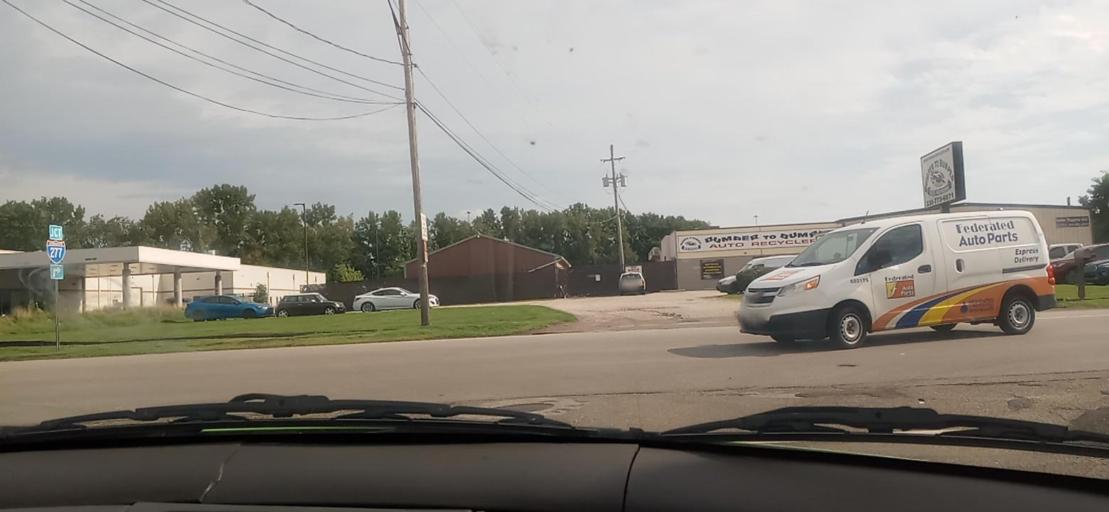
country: US
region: Ohio
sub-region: Summit County
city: Portage Lakes
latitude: 41.0289
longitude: -81.5293
